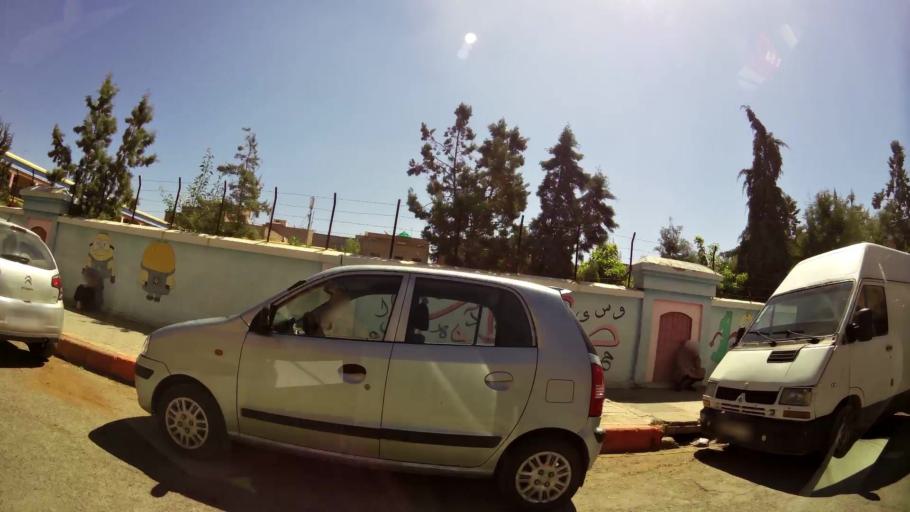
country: MA
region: Marrakech-Tensift-Al Haouz
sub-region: Marrakech
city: Marrakesh
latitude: 31.6339
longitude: -8.0695
